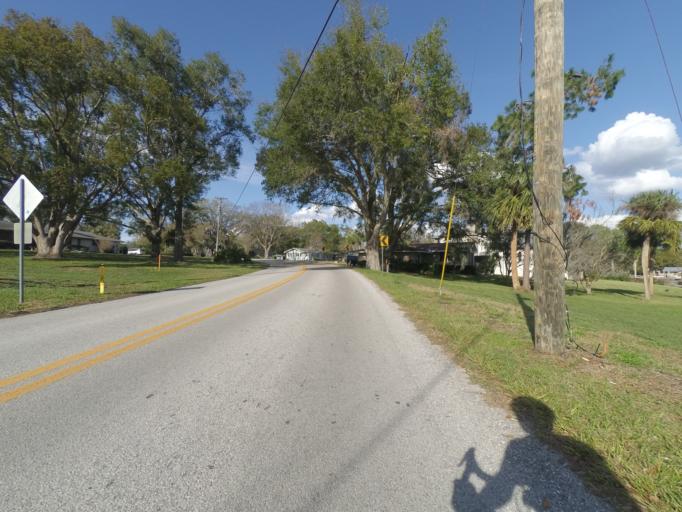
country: US
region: Florida
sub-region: Lake County
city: Mount Dora
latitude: 28.8197
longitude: -81.6622
